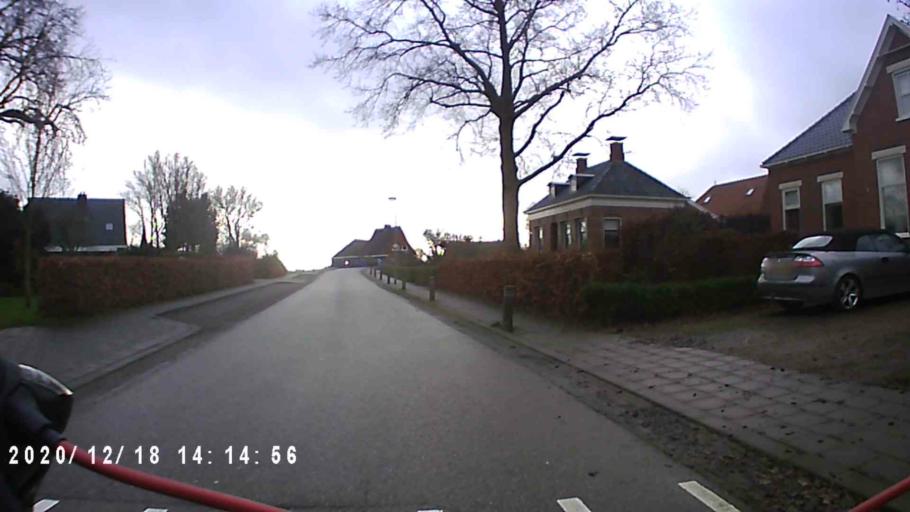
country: NL
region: Groningen
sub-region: Gemeente Bedum
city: Bedum
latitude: 53.2676
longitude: 6.6514
